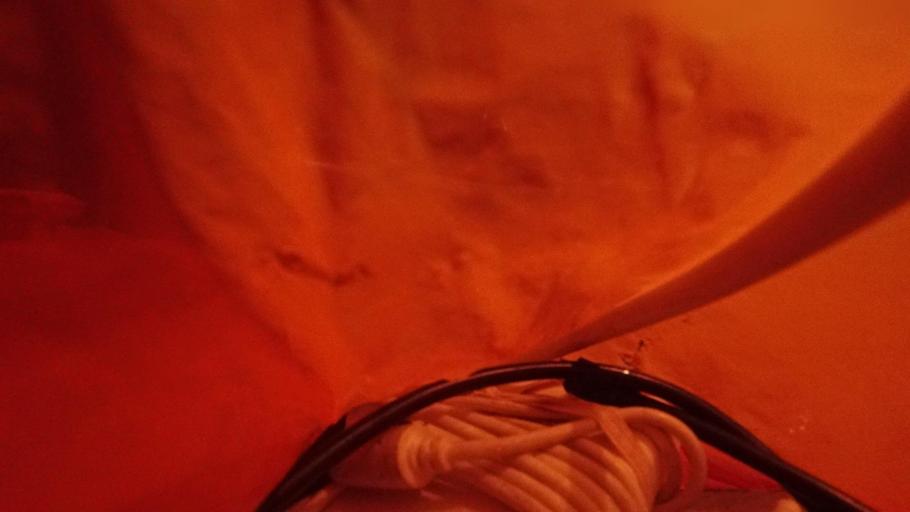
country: RU
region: Jewish Autonomous Oblast
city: Khingansk
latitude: 49.1630
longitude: 130.7704
